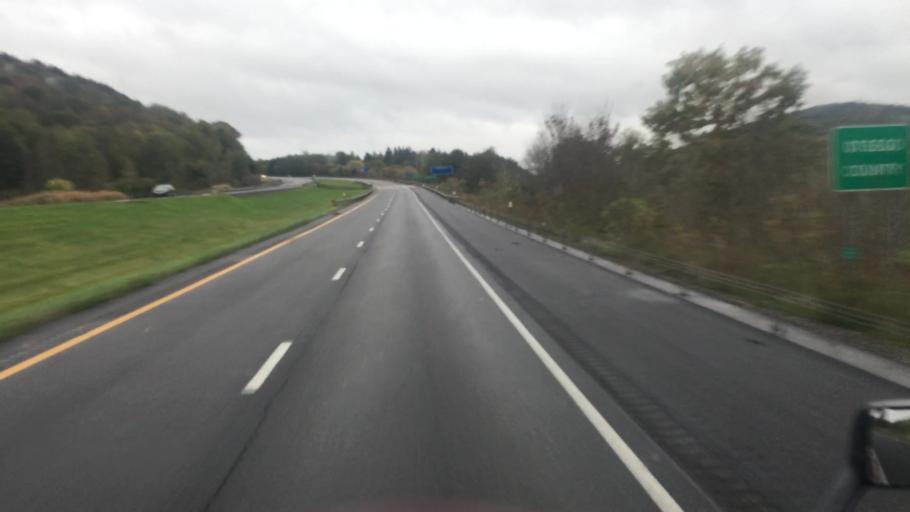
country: US
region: New York
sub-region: Otsego County
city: Unadilla
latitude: 42.3225
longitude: -75.3058
